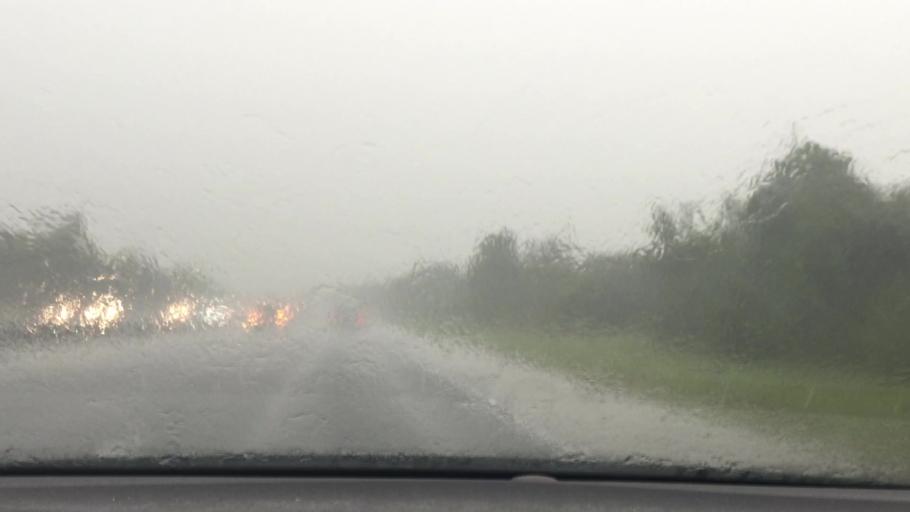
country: US
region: Florida
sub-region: Osceola County
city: Buenaventura Lakes
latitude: 28.3185
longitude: -81.3705
